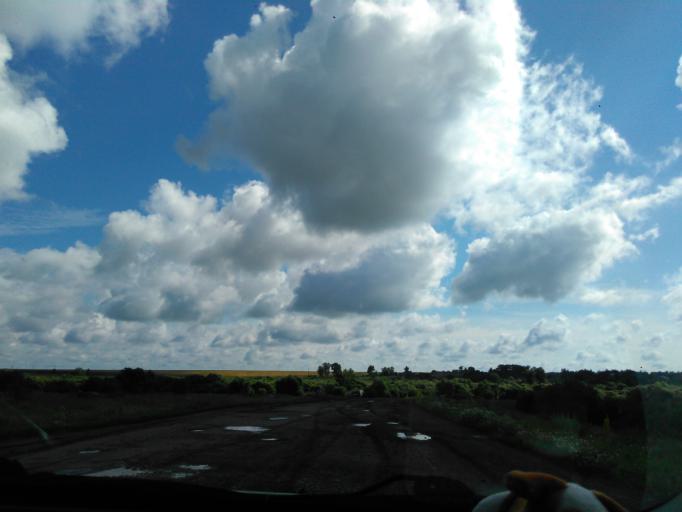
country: RU
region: Penza
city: Mokshan
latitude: 53.3535
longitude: 44.2398
